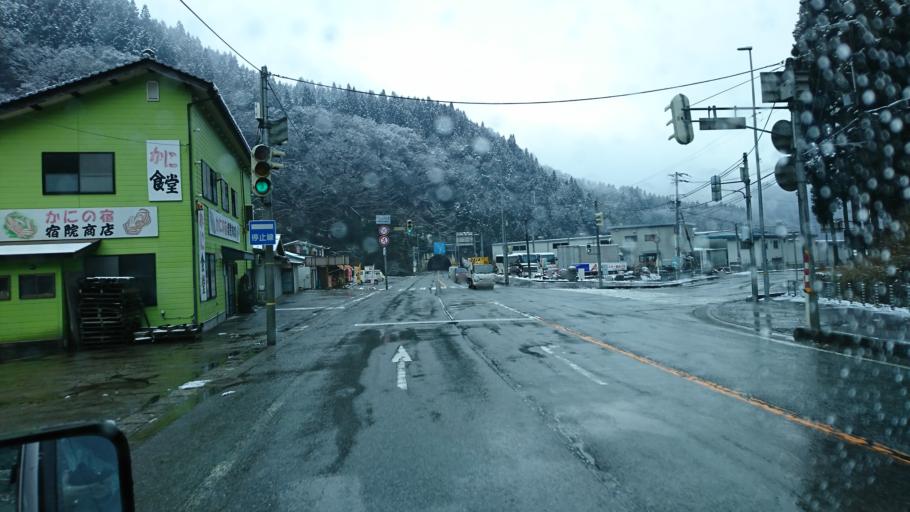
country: JP
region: Hyogo
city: Toyooka
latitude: 35.4900
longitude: 134.5699
